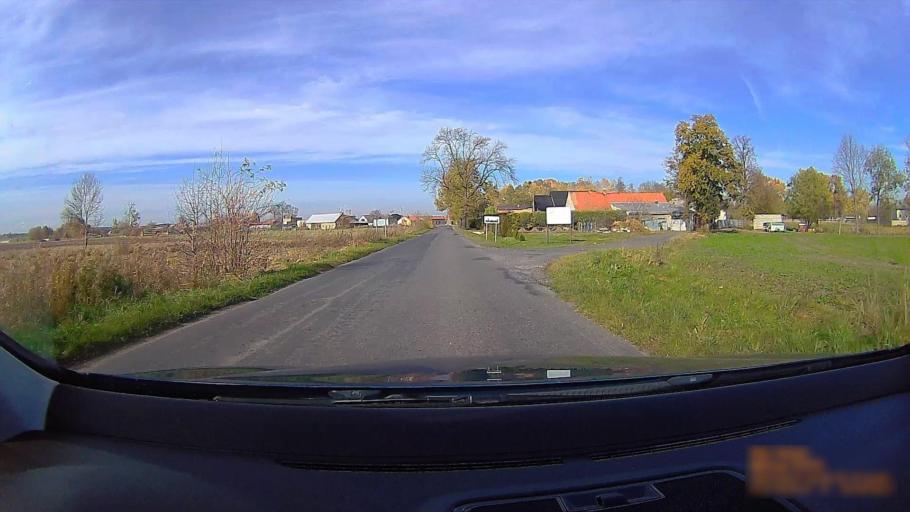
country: PL
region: Greater Poland Voivodeship
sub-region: Powiat ostrzeszowski
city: Doruchow
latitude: 51.4258
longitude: 18.0529
